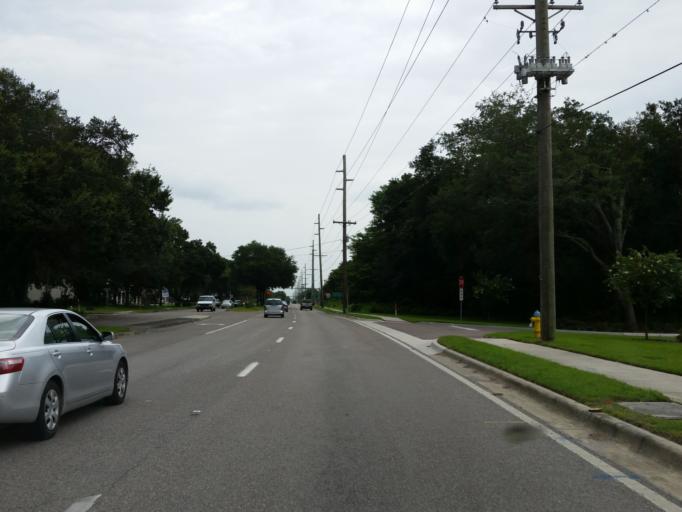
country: US
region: Florida
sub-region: Hillsborough County
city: Mango
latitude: 27.9693
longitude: -82.3352
